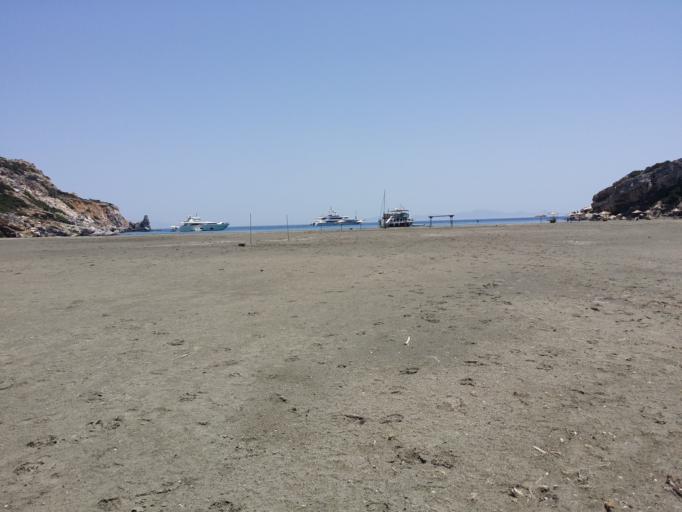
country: GR
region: South Aegean
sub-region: Nomos Kykladon
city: Antiparos
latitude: 36.9565
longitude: 24.9993
